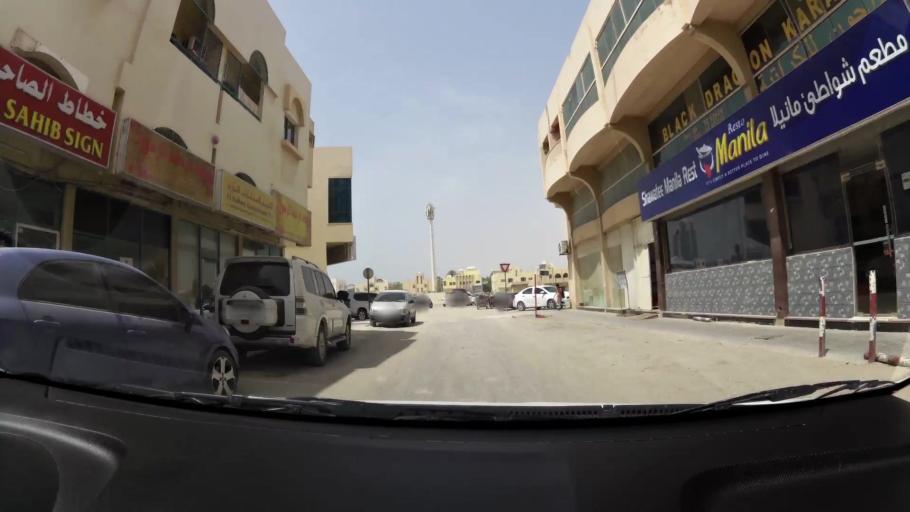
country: AE
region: Ash Shariqah
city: Sharjah
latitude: 25.3471
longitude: 55.3998
